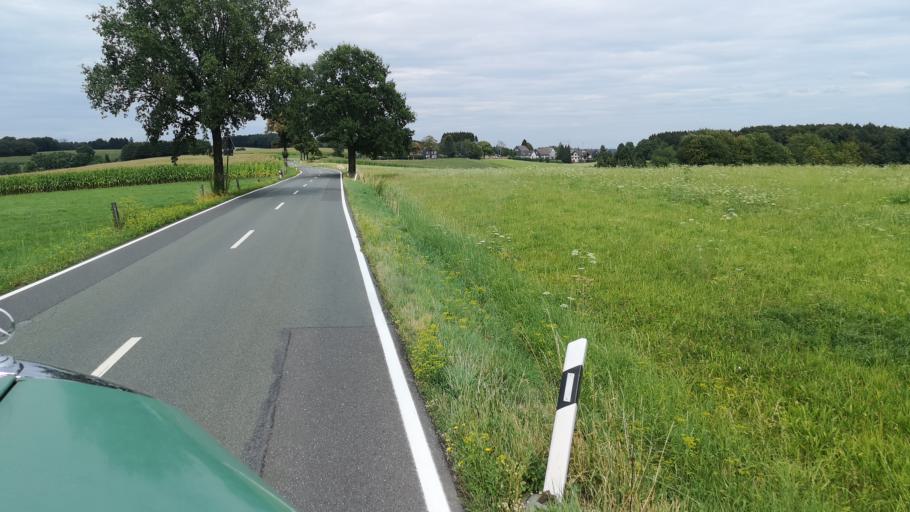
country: DE
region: North Rhine-Westphalia
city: Wermelskirchen
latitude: 51.1291
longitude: 7.2650
